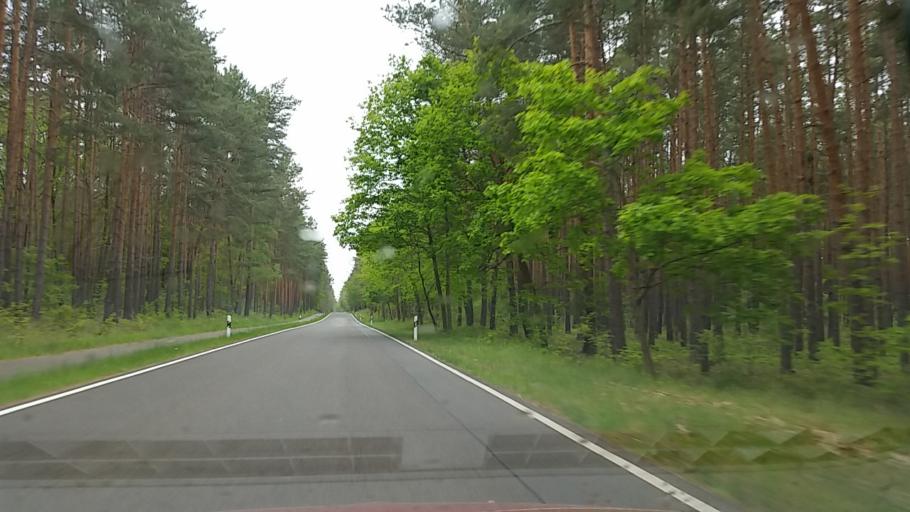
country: DE
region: Brandenburg
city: Reichenwalde
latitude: 52.3014
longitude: 13.9800
